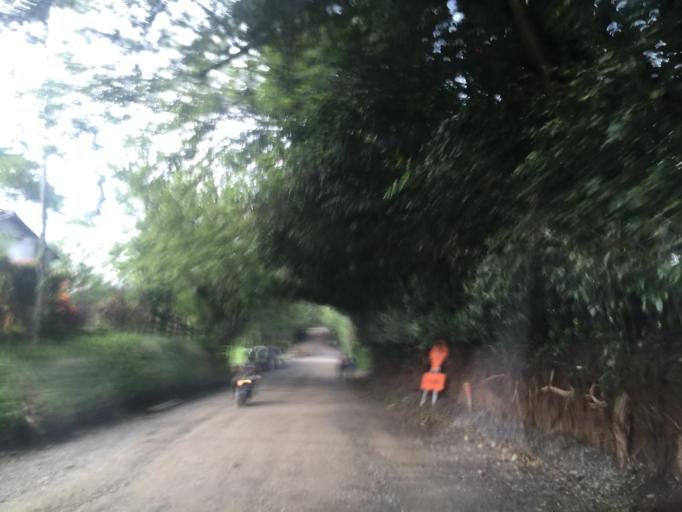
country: CO
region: Quindio
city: La Tebaida
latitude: 4.4609
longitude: -75.8024
